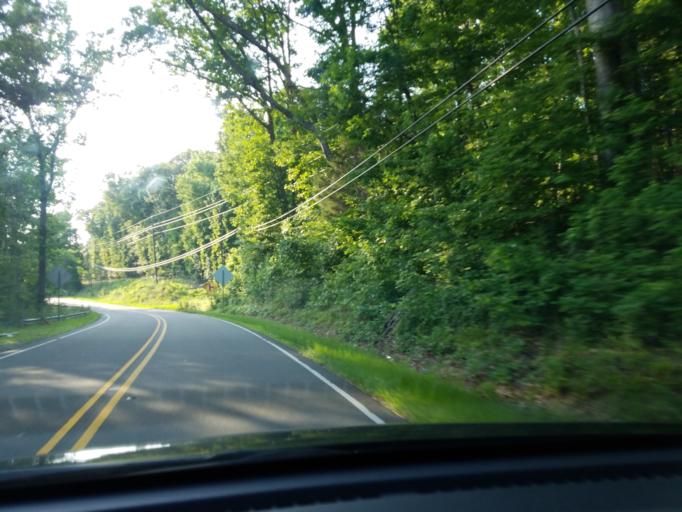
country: US
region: North Carolina
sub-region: Granville County
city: Butner
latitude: 36.1735
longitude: -78.8593
